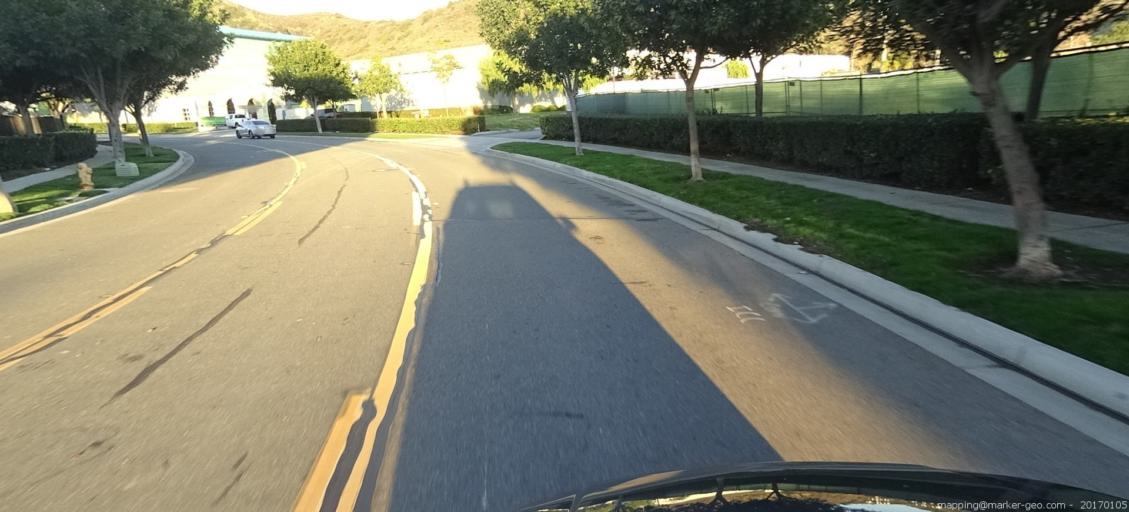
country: US
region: California
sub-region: Orange County
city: Ladera Ranch
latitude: 33.5562
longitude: -117.6286
